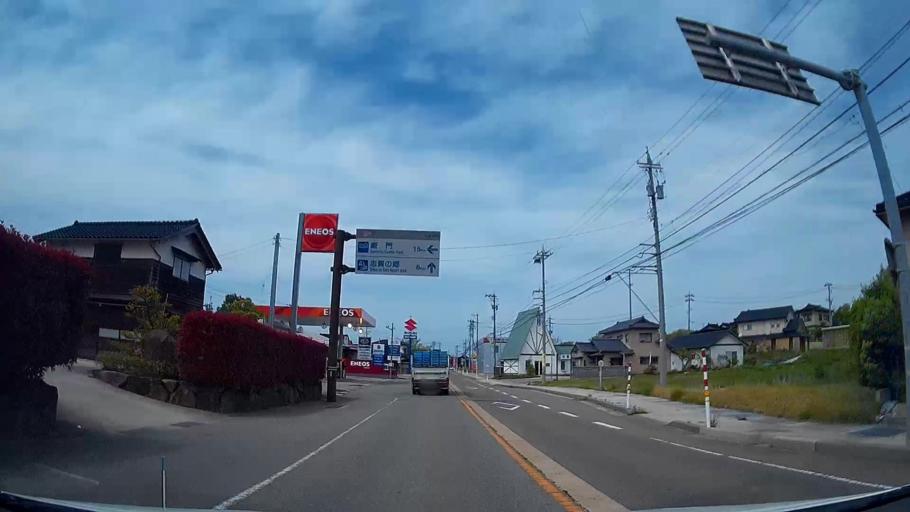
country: JP
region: Ishikawa
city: Hakui
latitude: 36.9941
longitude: 136.7767
